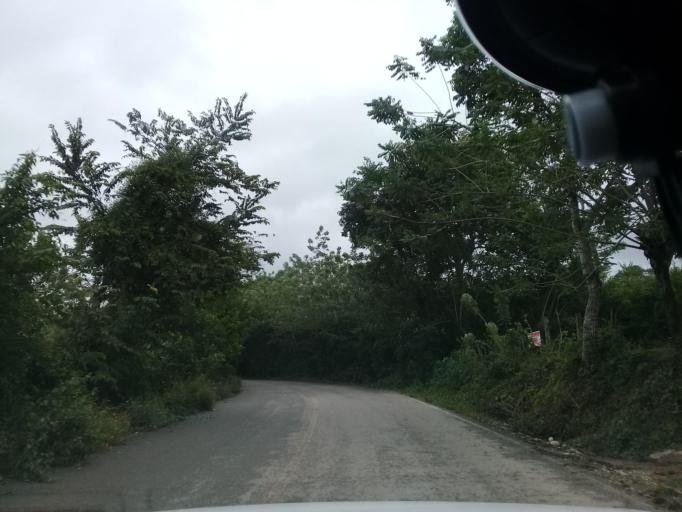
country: MX
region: Veracruz
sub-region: Chalma
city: San Pedro Coyutla
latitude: 21.2079
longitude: -98.4059
